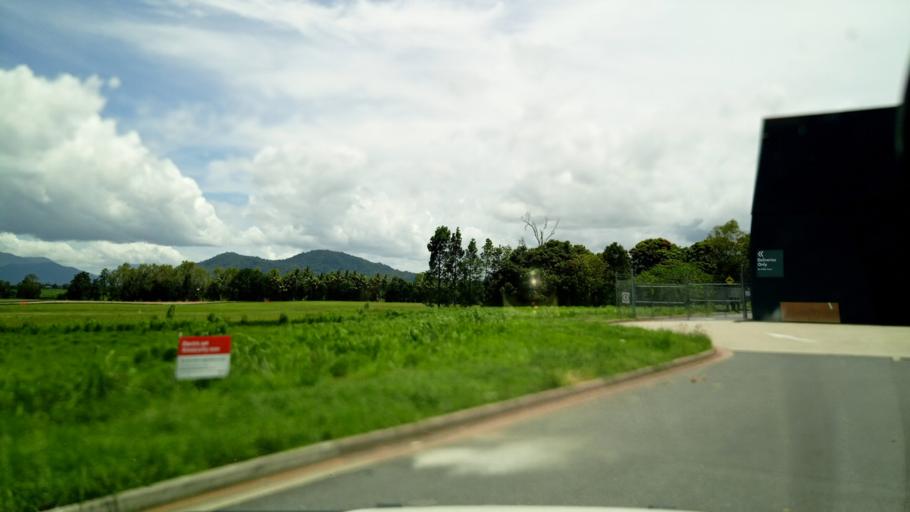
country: AU
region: Queensland
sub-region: Cairns
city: Redlynch
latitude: -16.8404
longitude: 145.6959
